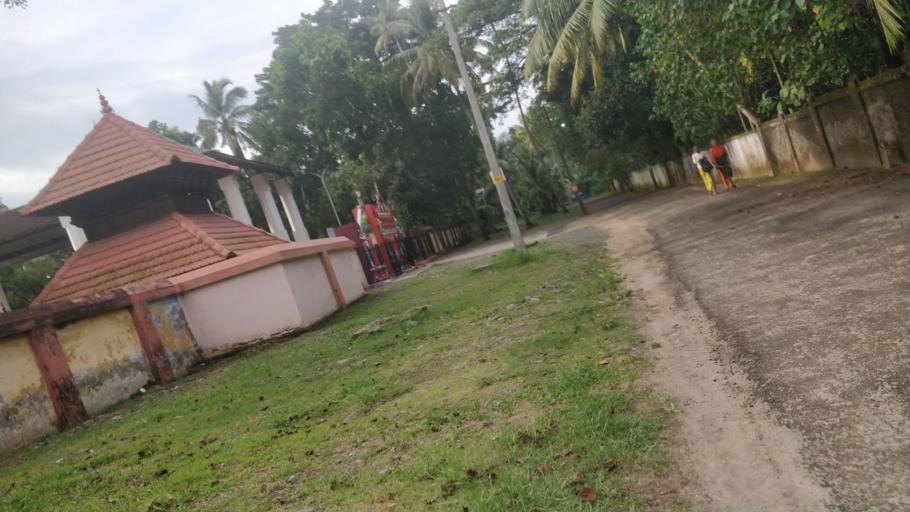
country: IN
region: Kerala
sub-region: Alappuzha
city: Shertallai
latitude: 9.6961
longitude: 76.3624
